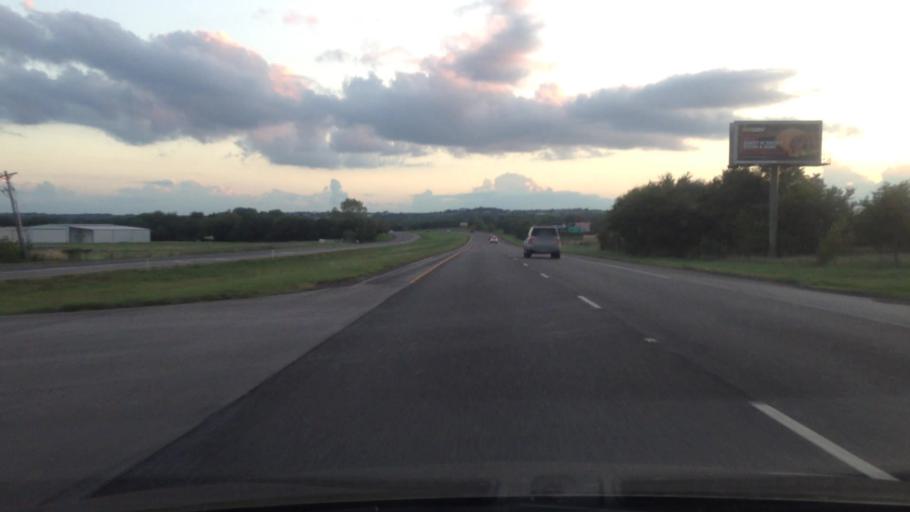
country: US
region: Texas
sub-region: Parker County
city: Aledo
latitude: 32.5893
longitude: -97.5900
